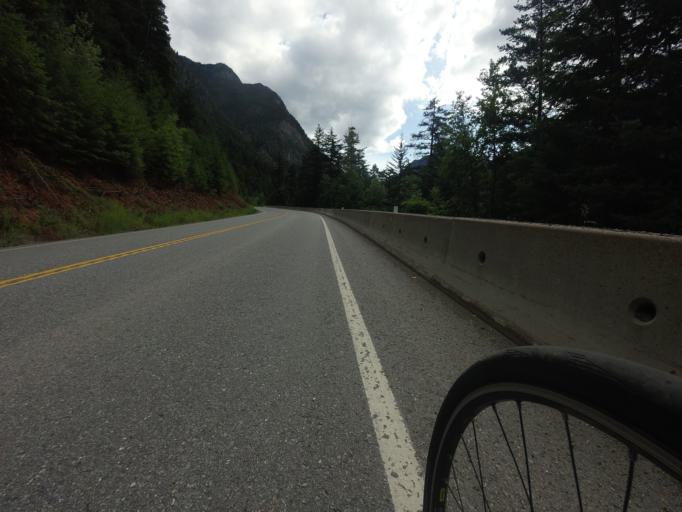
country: CA
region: British Columbia
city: Lillooet
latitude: 50.6336
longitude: -122.0889
